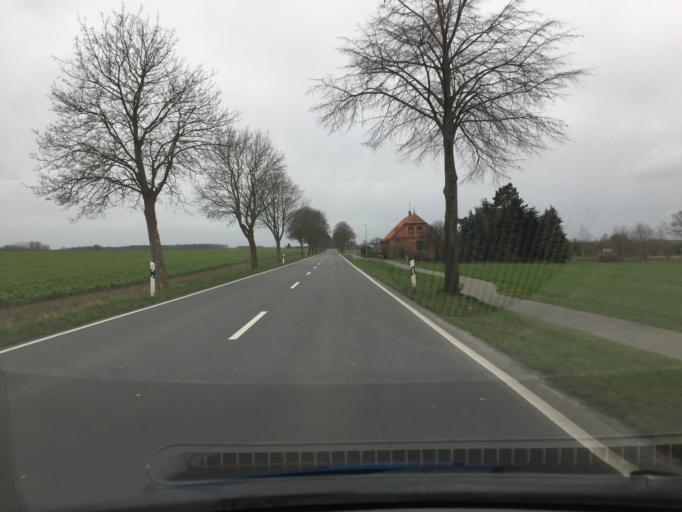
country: DE
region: Lower Saxony
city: Oetzen
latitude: 53.0044
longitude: 10.6710
